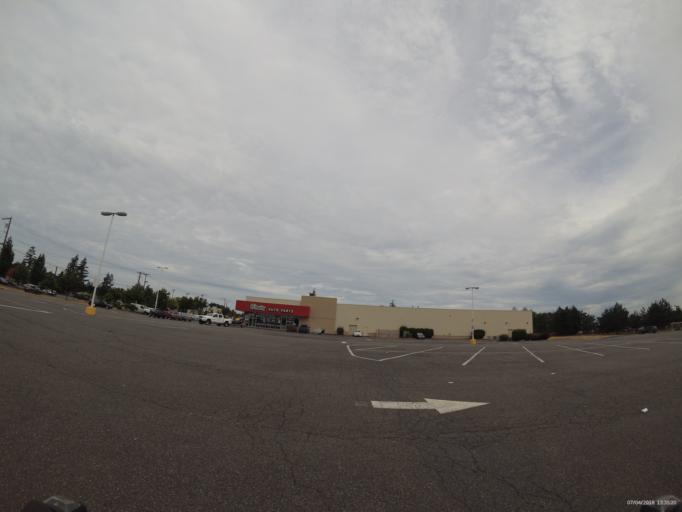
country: US
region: Washington
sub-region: Pierce County
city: McChord Air Force Base
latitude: 47.1579
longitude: -122.4884
